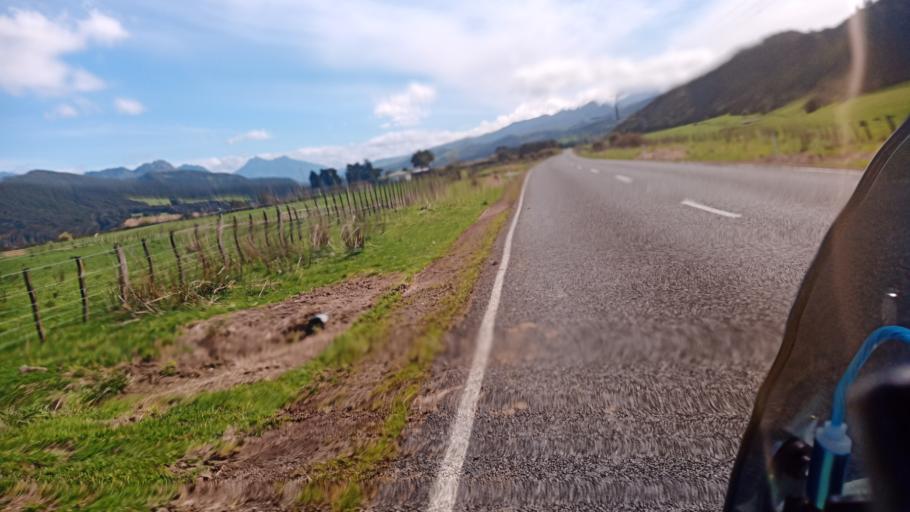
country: NZ
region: Gisborne
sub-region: Gisborne District
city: Gisborne
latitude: -37.8770
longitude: 178.2875
